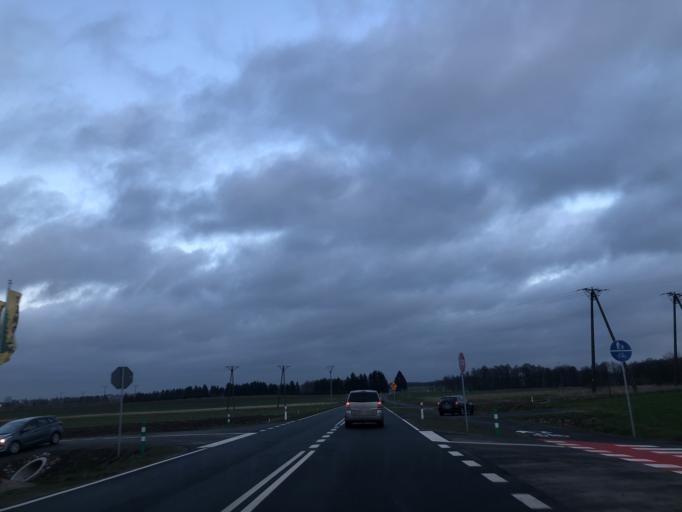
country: PL
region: Podlasie
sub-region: Lomza
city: Lomza
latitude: 53.1231
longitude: 22.0399
